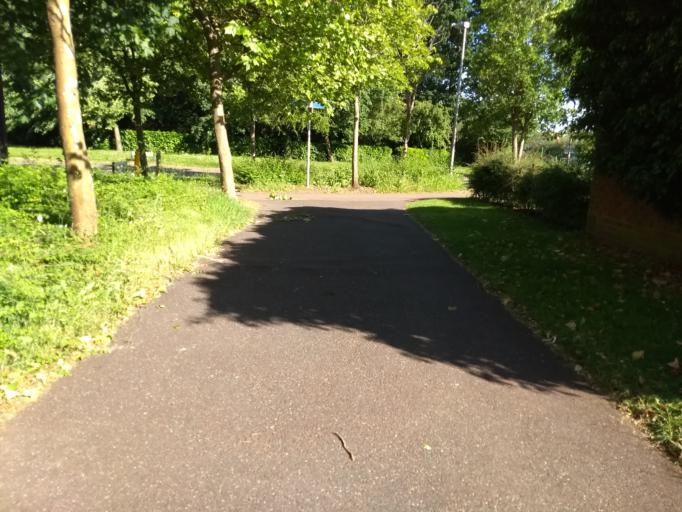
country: GB
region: England
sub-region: Milton Keynes
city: Shenley Church End
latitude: 52.0181
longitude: -0.7764
